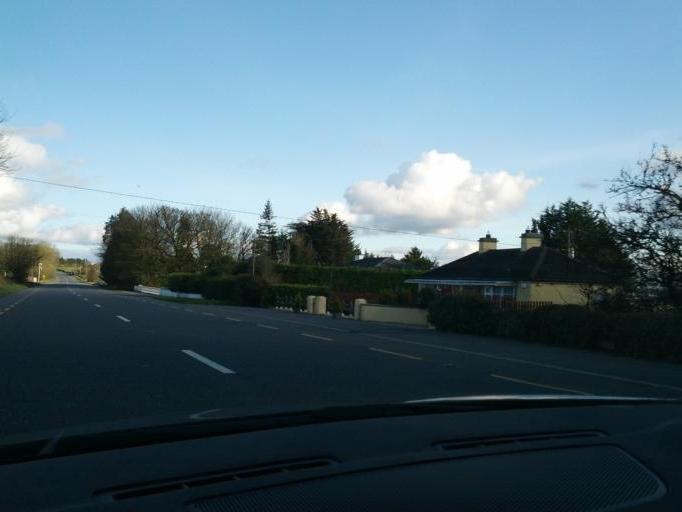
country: IE
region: Connaught
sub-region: Roscommon
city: Castlerea
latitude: 53.6836
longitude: -8.3590
